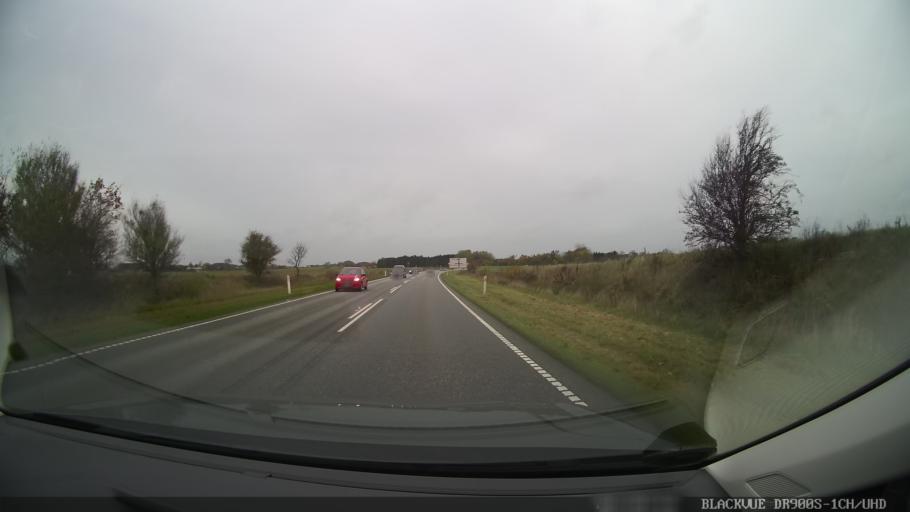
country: DK
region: North Denmark
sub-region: Thisted Kommune
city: Thisted
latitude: 56.8282
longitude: 8.7174
